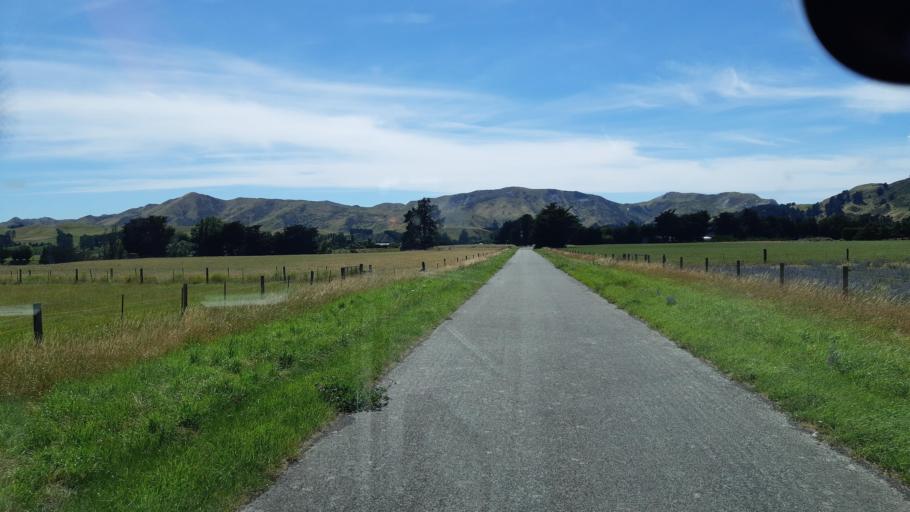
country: NZ
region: Marlborough
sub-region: Marlborough District
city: Blenheim
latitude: -41.8278
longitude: 174.1238
